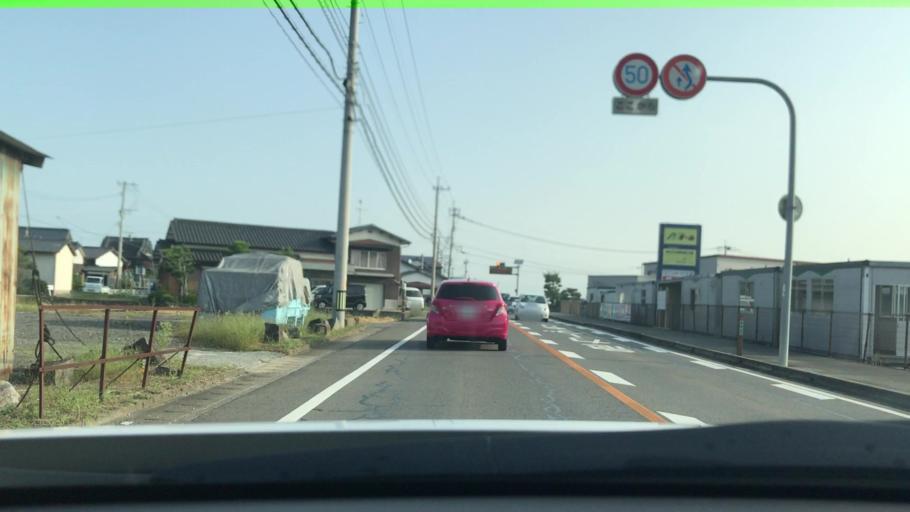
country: JP
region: Saga Prefecture
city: Saga-shi
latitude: 33.2012
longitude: 130.2032
